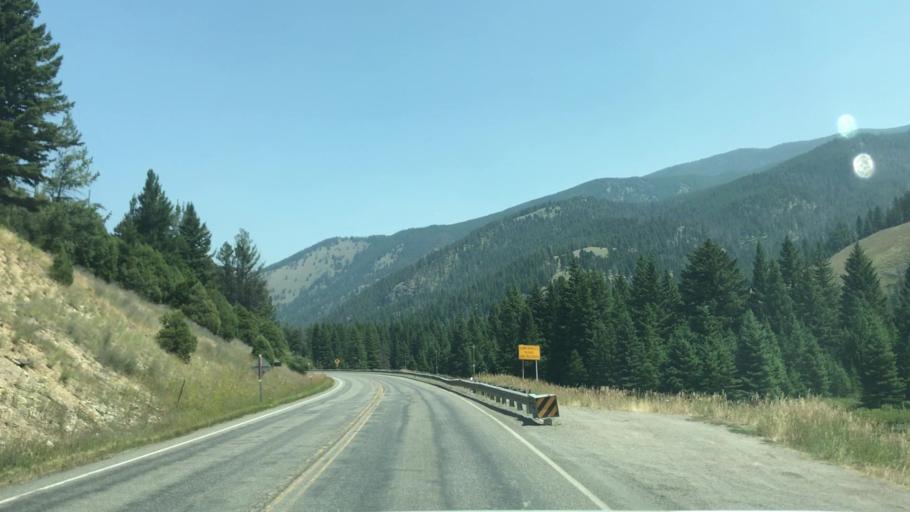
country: US
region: Montana
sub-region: Gallatin County
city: Big Sky
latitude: 45.2702
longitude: -111.2460
